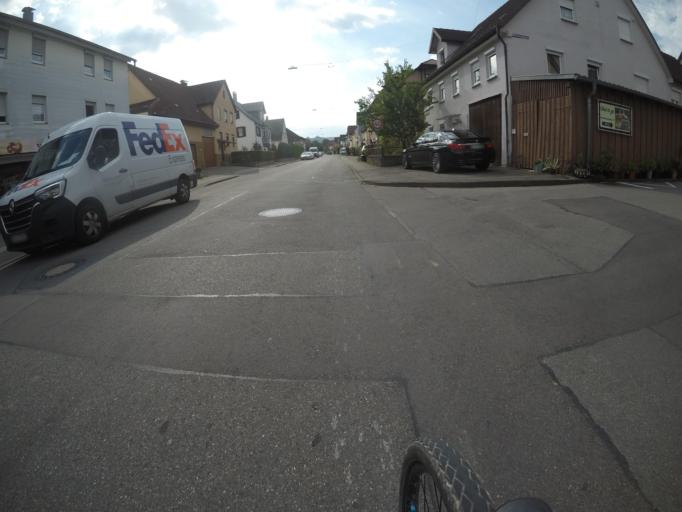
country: DE
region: Baden-Wuerttemberg
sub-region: Tuebingen Region
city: Dettingen an der Erms
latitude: 48.5280
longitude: 9.3522
